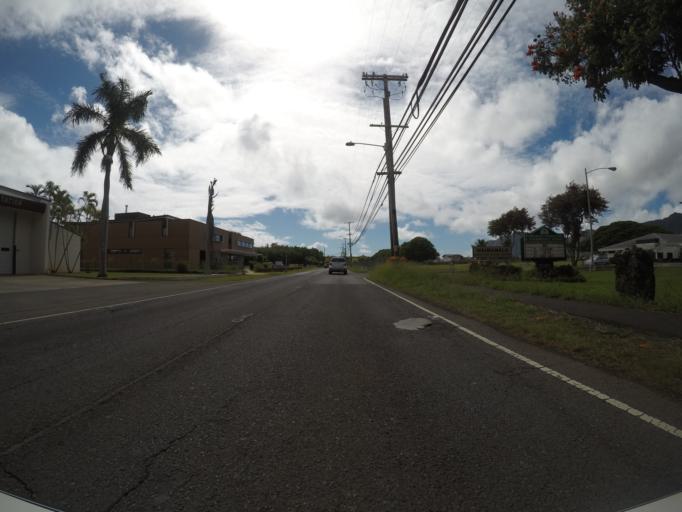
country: US
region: Hawaii
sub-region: Honolulu County
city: Waimanalo
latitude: 21.3469
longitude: -157.7151
